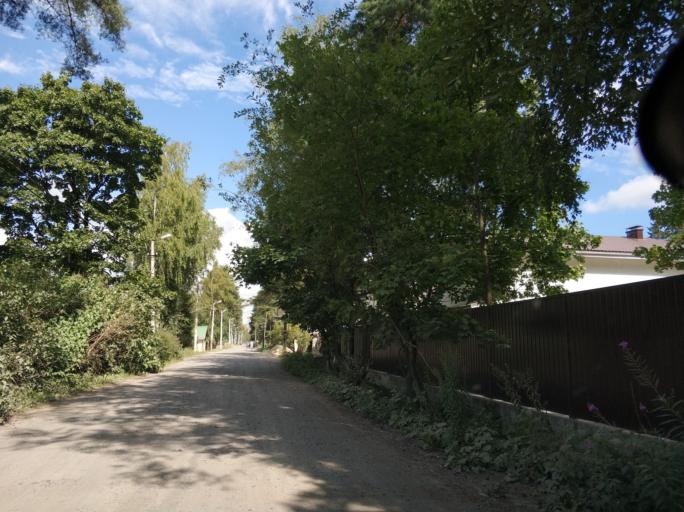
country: RU
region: Leningrad
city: Vsevolozhsk
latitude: 60.0198
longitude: 30.6163
